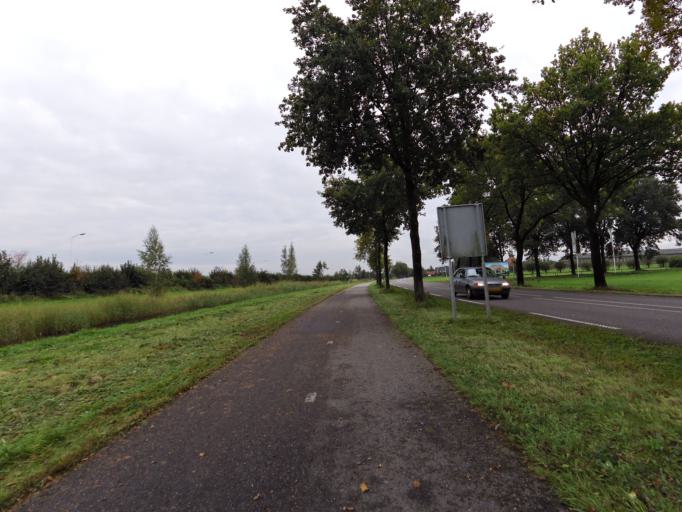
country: NL
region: Gelderland
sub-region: Oude IJsselstreek
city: Gendringen
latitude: 51.9049
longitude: 6.3539
